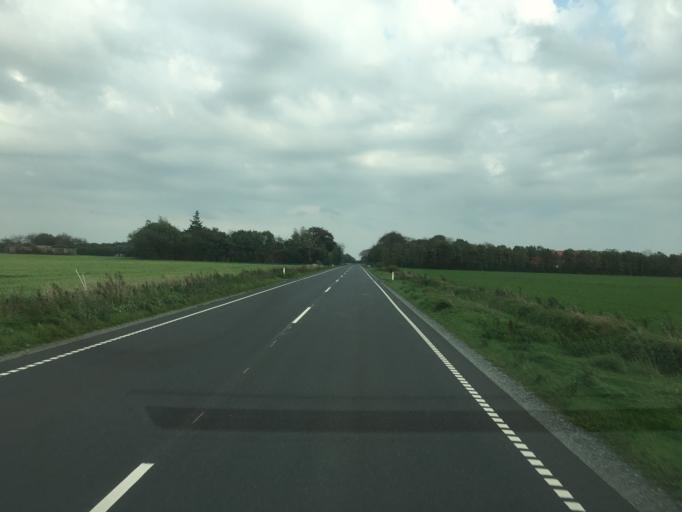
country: DK
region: South Denmark
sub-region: Tonder Kommune
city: Logumkloster
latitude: 54.9789
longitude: 9.0321
